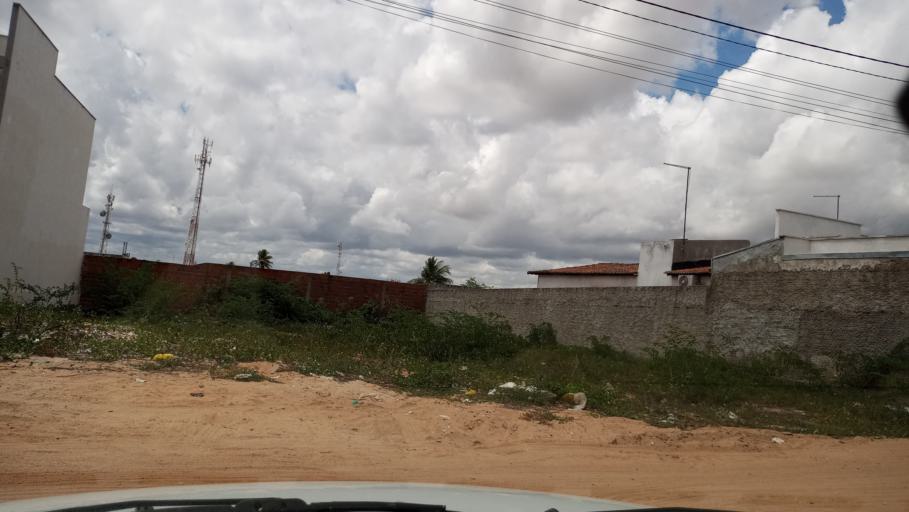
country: BR
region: Rio Grande do Norte
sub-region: Joao Camara
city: Joao Camara
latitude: -5.5360
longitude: -35.8127
